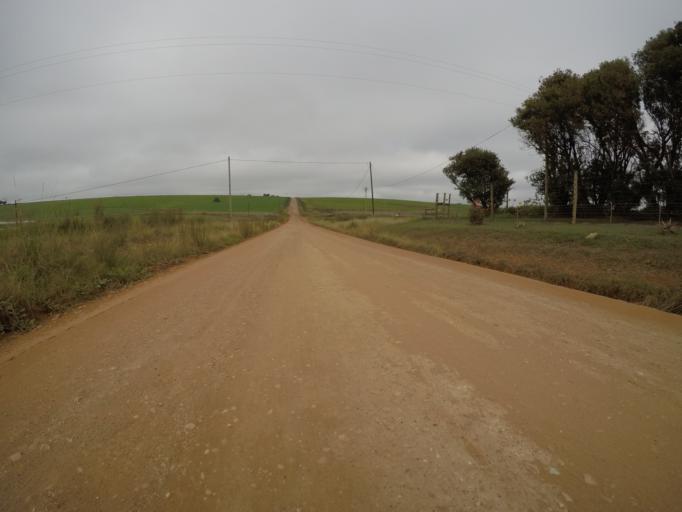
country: ZA
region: Eastern Cape
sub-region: Cacadu District Municipality
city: Kareedouw
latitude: -34.0172
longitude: 24.2388
